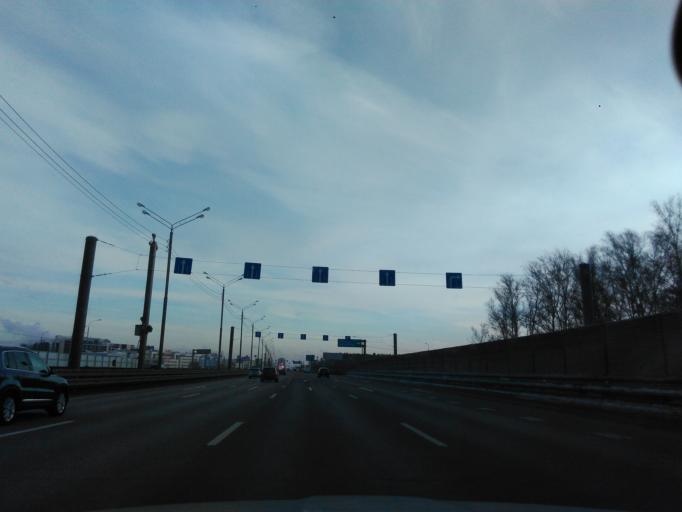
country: RU
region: Moskovskaya
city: Opalikha
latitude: 55.7792
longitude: 37.2355
